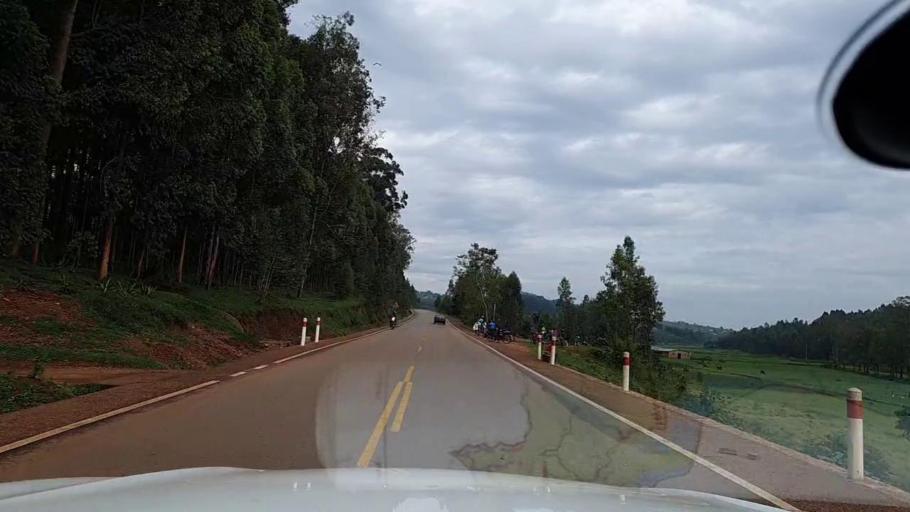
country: RW
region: Southern Province
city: Butare
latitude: -2.5622
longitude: 29.7218
